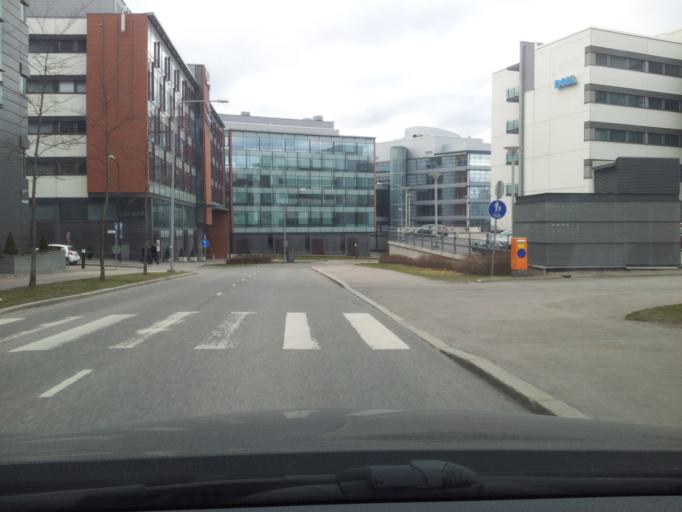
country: FI
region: Uusimaa
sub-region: Helsinki
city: Kilo
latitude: 60.2126
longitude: 24.8113
